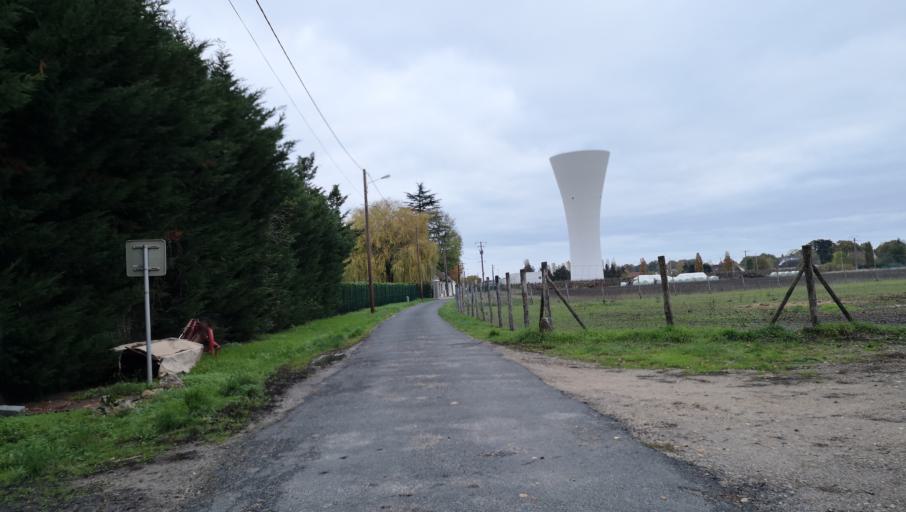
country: FR
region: Centre
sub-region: Departement du Loiret
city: Semoy
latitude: 47.9179
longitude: 1.9566
